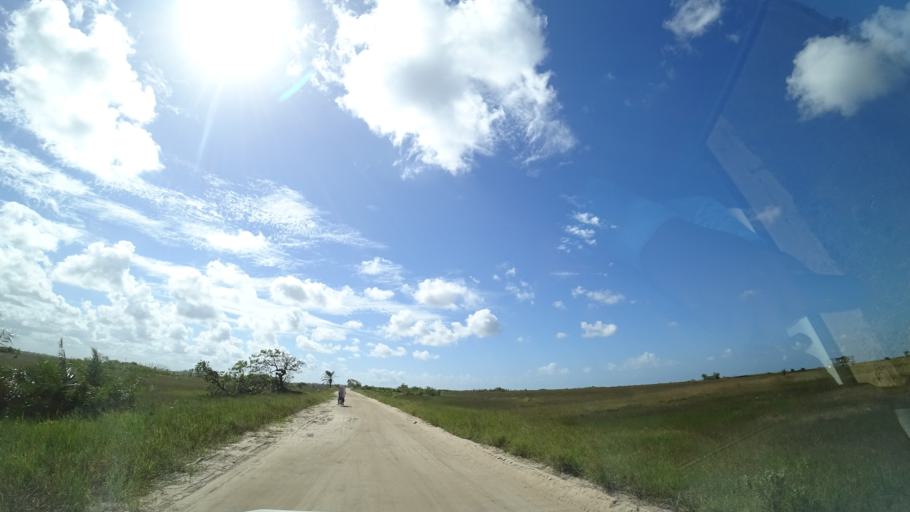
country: MZ
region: Sofala
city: Beira
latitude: -19.7503
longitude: 34.9387
